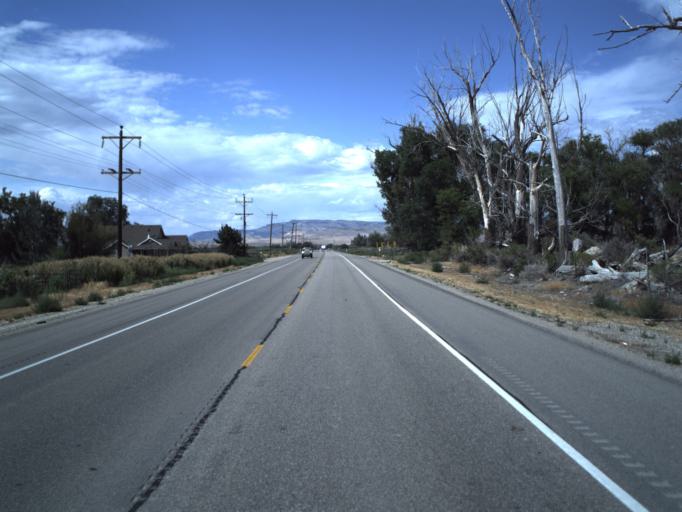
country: US
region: Utah
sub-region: Sanpete County
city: Centerfield
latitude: 39.0955
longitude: -111.8198
